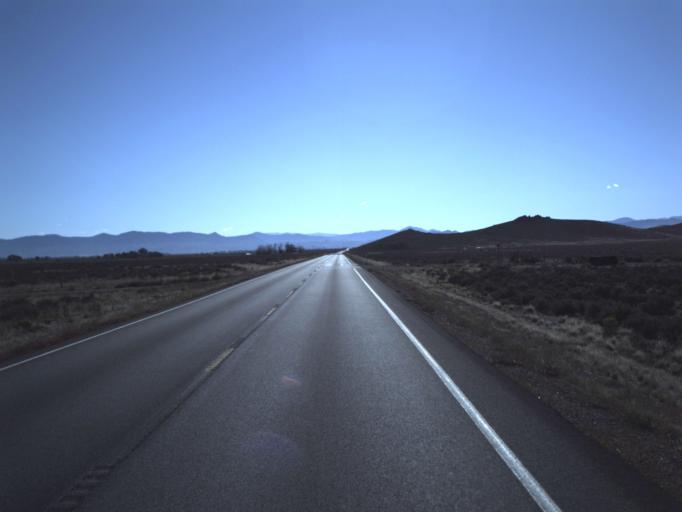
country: US
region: Utah
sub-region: Washington County
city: Enterprise
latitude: 37.7491
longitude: -113.7671
